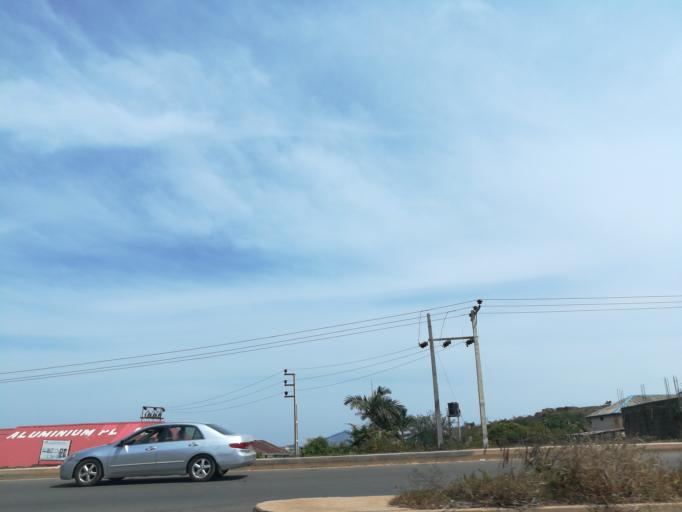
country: NG
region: Plateau
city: Bukuru
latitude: 9.8327
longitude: 8.8671
